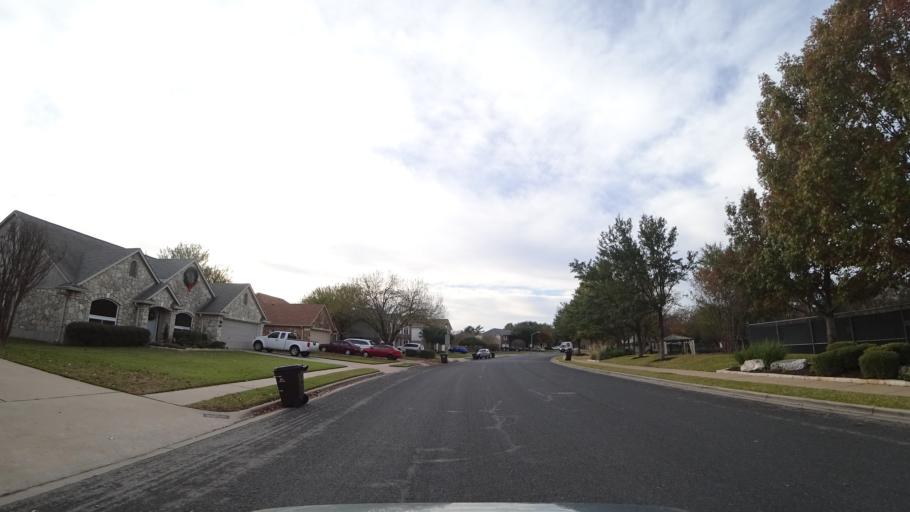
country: US
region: Texas
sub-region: Williamson County
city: Brushy Creek
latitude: 30.5156
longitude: -97.7221
